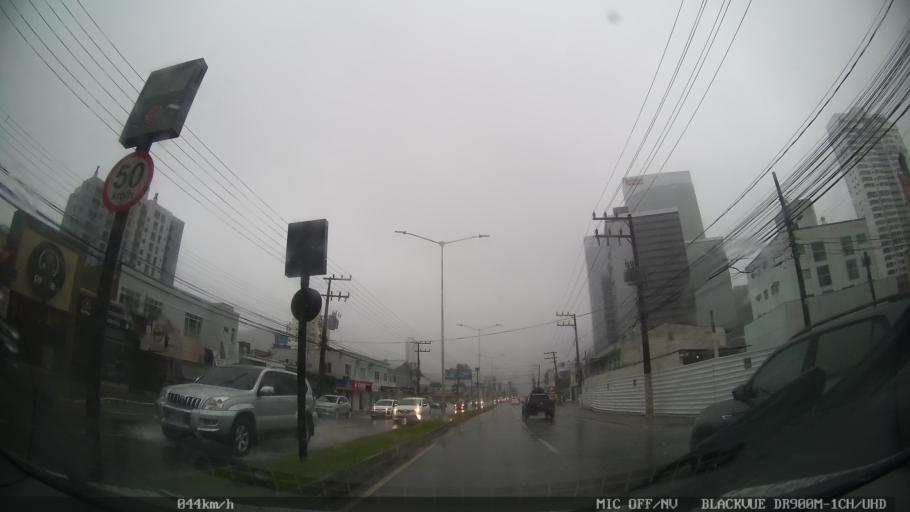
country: BR
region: Santa Catarina
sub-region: Balneario Camboriu
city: Balneario Camboriu
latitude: -26.9547
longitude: -48.6403
